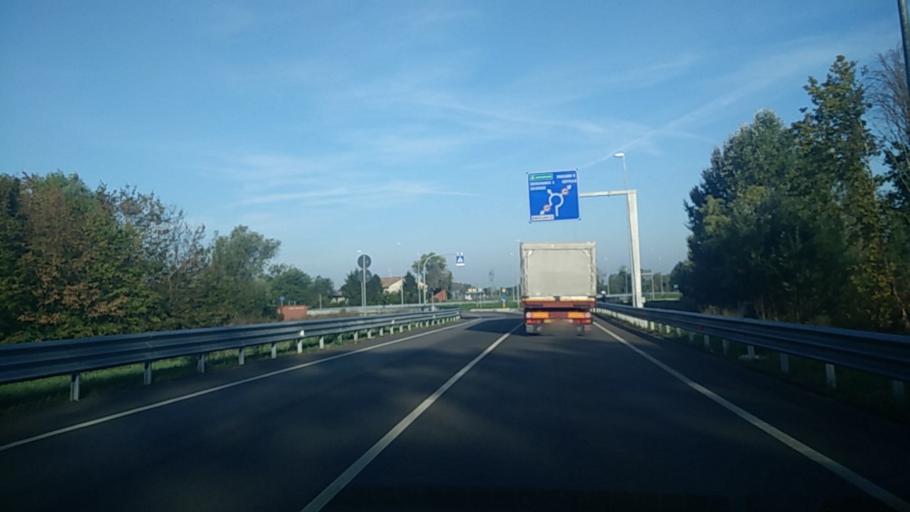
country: IT
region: Veneto
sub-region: Provincia di Venezia
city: Martellago
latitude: 45.5536
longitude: 12.1631
